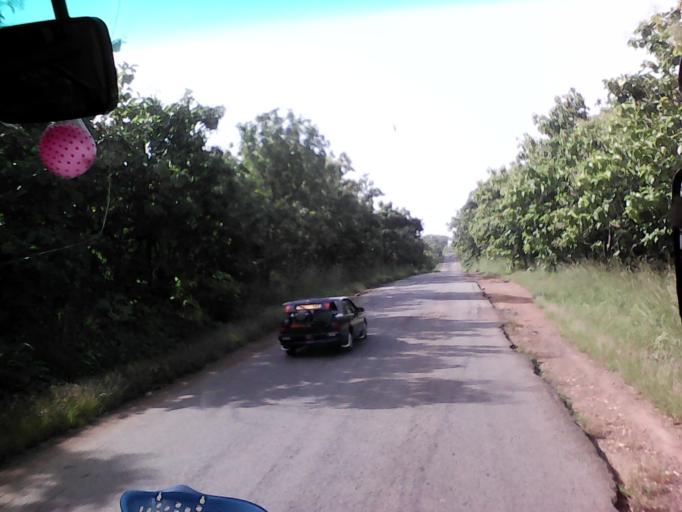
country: TG
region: Centrale
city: Sokode
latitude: 9.1255
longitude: 1.1472
